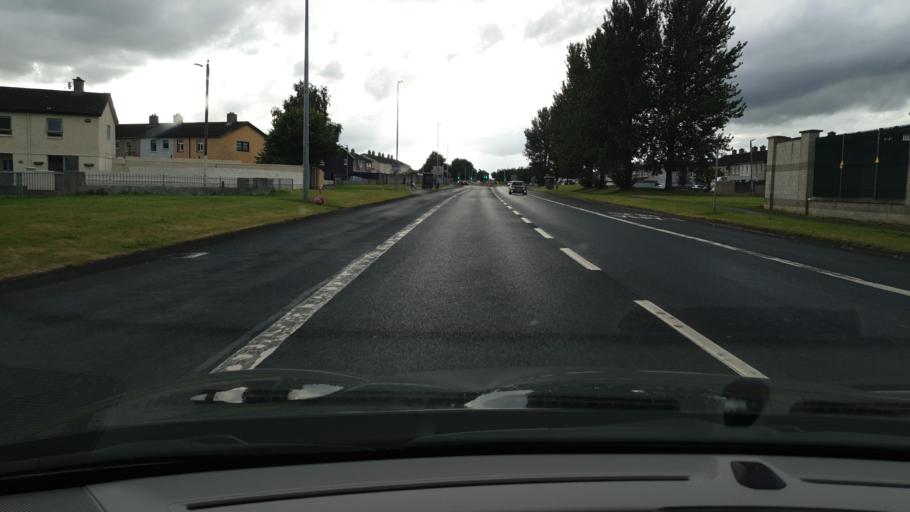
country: IE
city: Palmerstown
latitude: 53.3478
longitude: -6.3936
